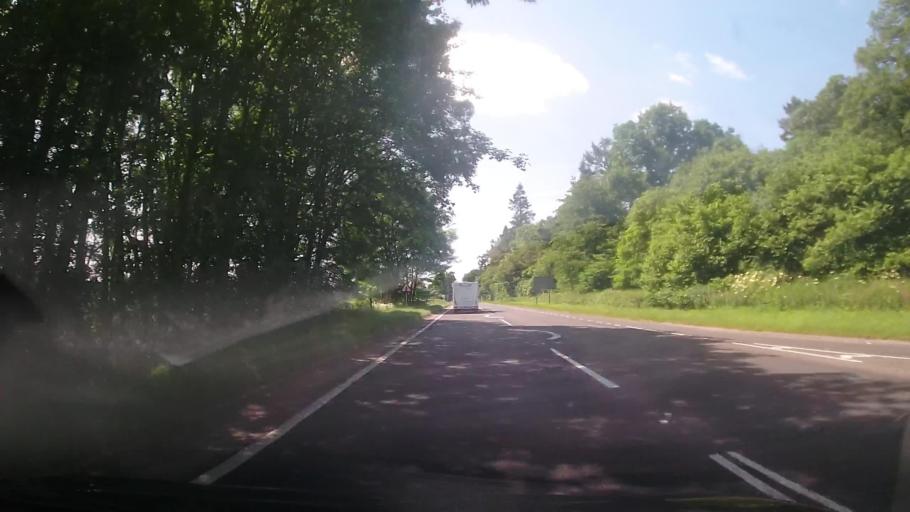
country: GB
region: England
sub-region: Shropshire
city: Ludlow
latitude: 52.3390
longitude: -2.7105
